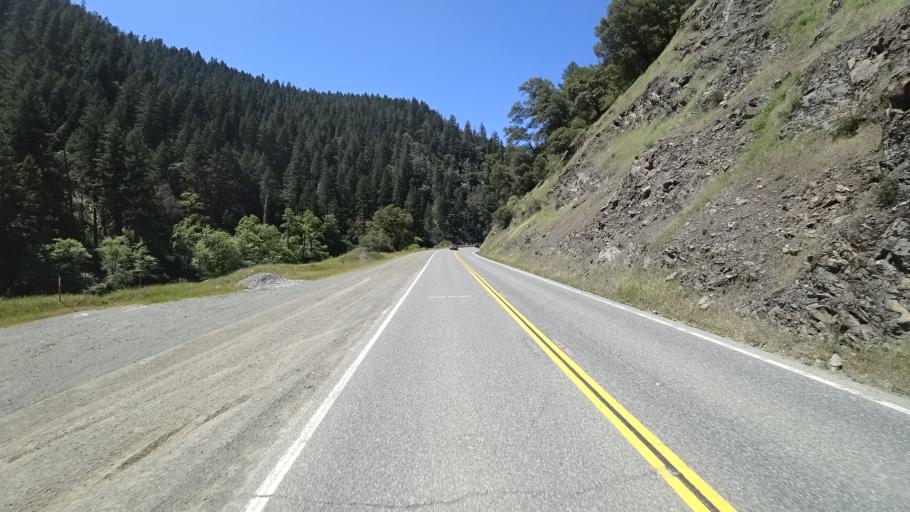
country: US
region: California
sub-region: Trinity County
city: Hayfork
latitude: 40.7722
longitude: -123.3099
